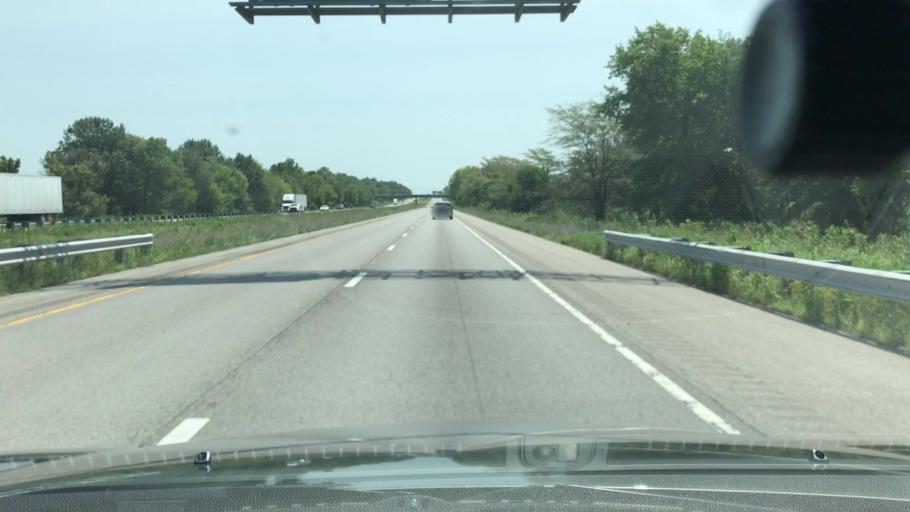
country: US
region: Illinois
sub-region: Jefferson County
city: Mount Vernon
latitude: 38.3453
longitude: -88.9760
